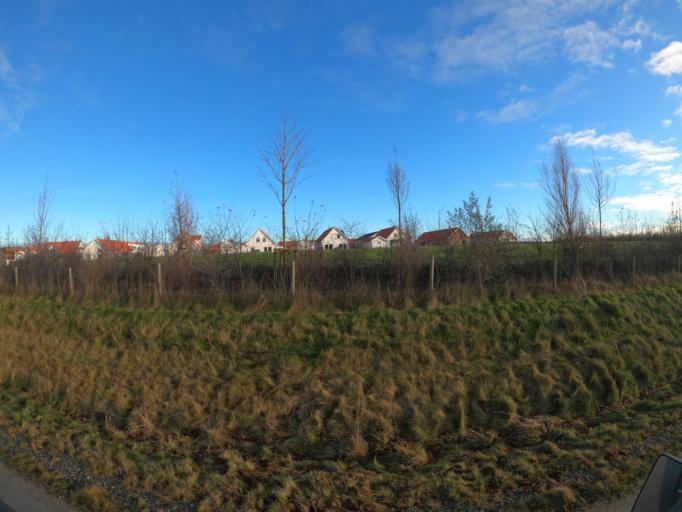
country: SE
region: Skane
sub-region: Svedala Kommun
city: Svedala
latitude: 55.4974
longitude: 13.2377
